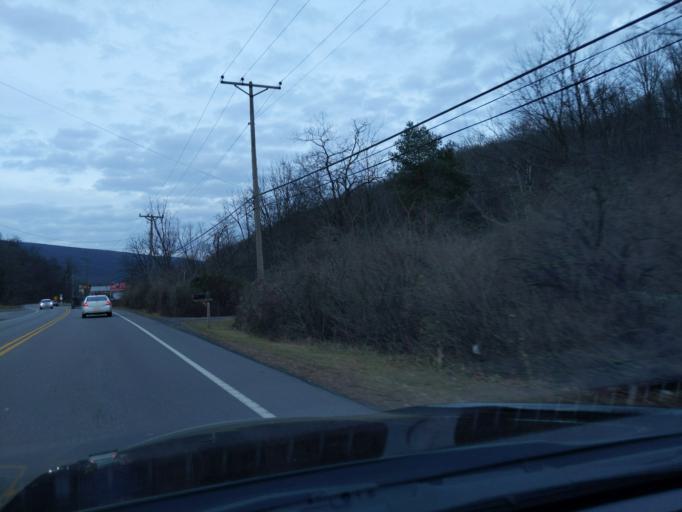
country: US
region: Pennsylvania
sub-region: Blair County
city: Hollidaysburg
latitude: 40.4469
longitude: -78.3535
